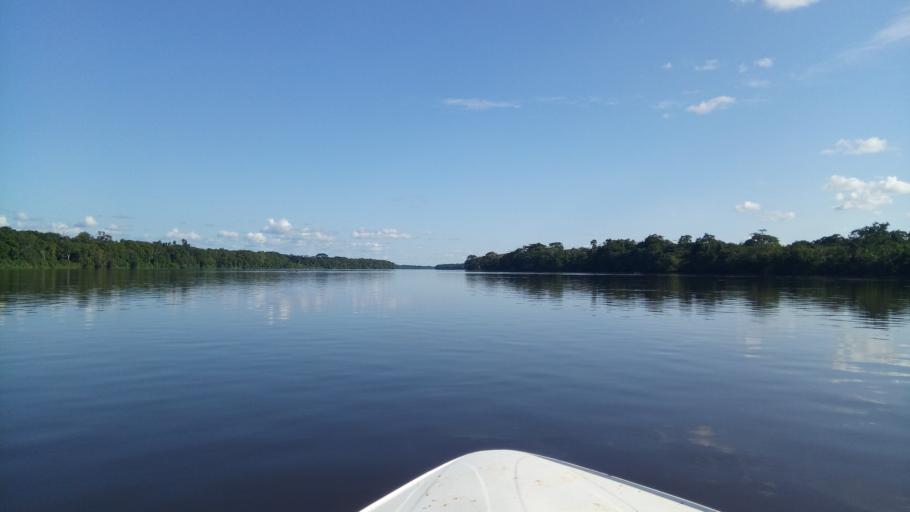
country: CD
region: Eastern Province
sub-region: Sous-Region de la Tshopo
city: Yangambi
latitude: 0.4435
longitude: 24.1629
